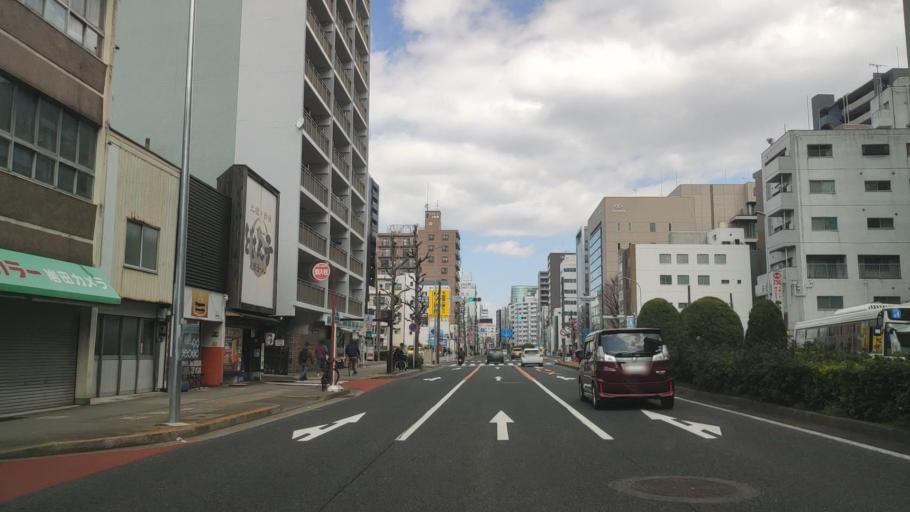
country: JP
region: Aichi
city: Nagoya-shi
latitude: 35.1540
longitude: 136.9052
